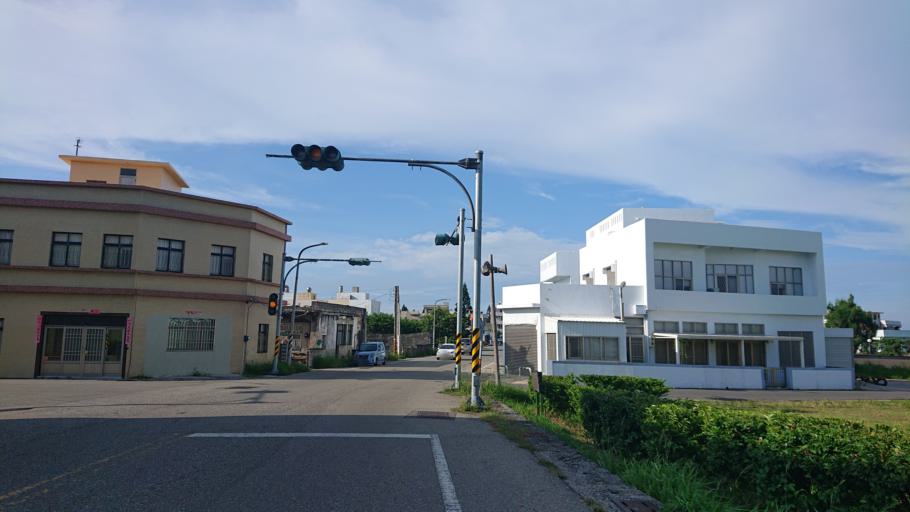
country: TW
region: Taiwan
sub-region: Penghu
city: Ma-kung
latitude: 23.5250
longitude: 119.6021
